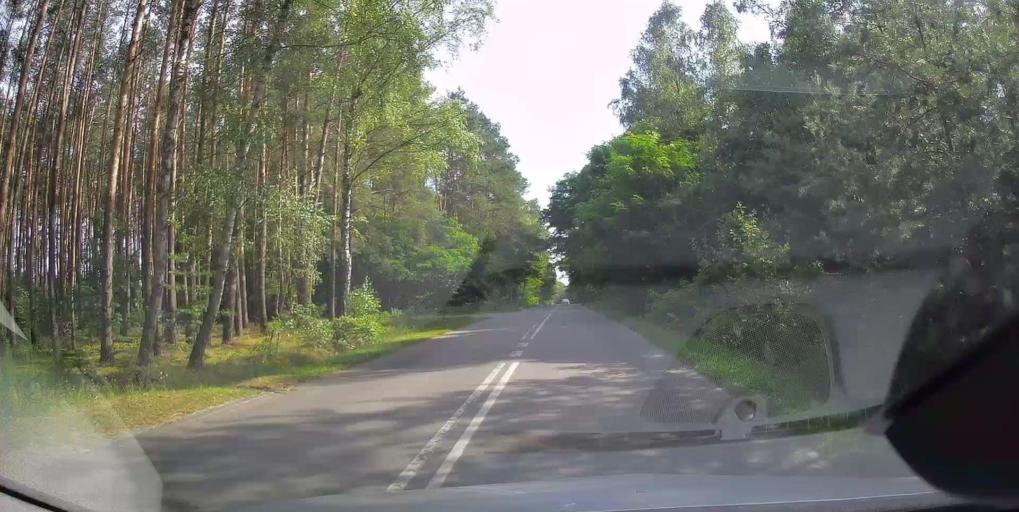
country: PL
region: Lodz Voivodeship
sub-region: Powiat opoczynski
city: Mniszkow
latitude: 51.4006
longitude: 20.0382
